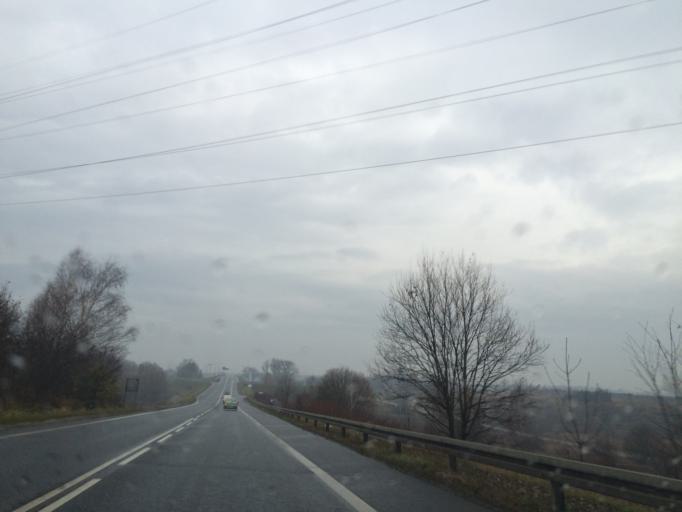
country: PL
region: Silesian Voivodeship
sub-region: Piekary Slaskie
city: Piekary Slaskie
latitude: 50.3683
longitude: 18.9054
